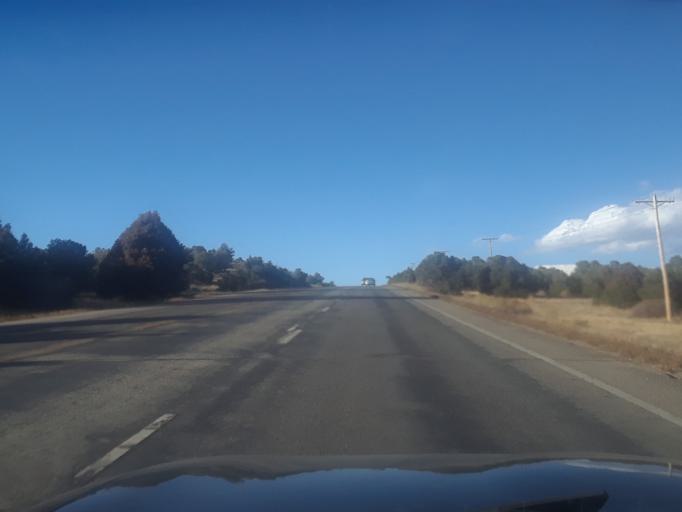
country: US
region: Colorado
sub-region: Chaffee County
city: Salida
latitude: 38.6559
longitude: -106.0862
